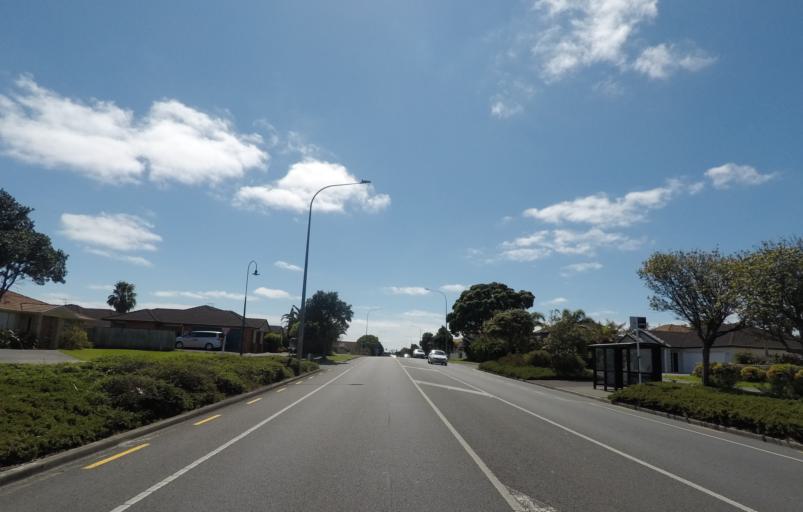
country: NZ
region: Auckland
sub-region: Auckland
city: Manukau City
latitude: -36.9459
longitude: 174.9118
